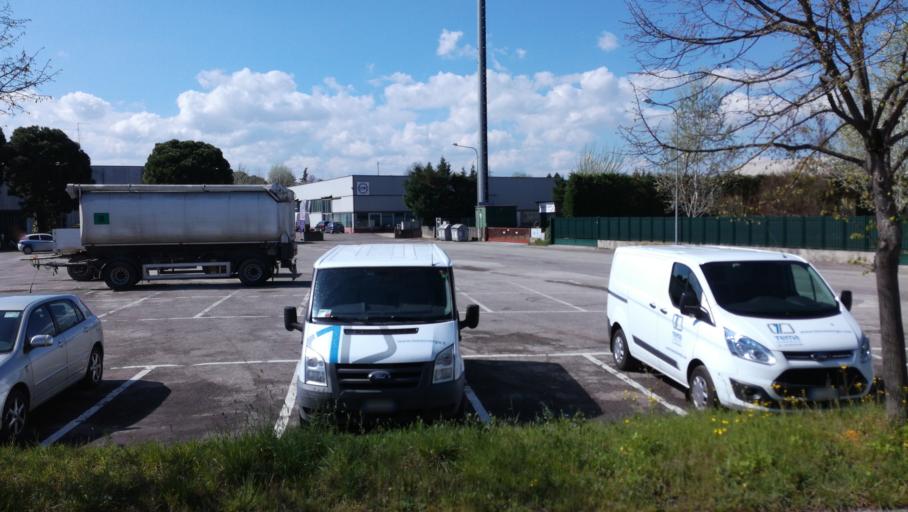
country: IT
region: Emilia-Romagna
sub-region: Provincia di Ravenna
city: Faenza
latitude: 44.2993
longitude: 11.8725
